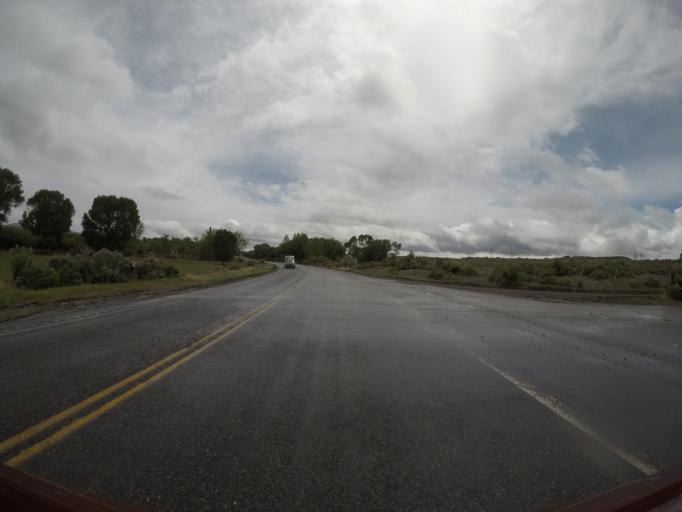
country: US
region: Wyoming
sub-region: Big Horn County
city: Lovell
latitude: 44.8645
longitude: -108.3313
